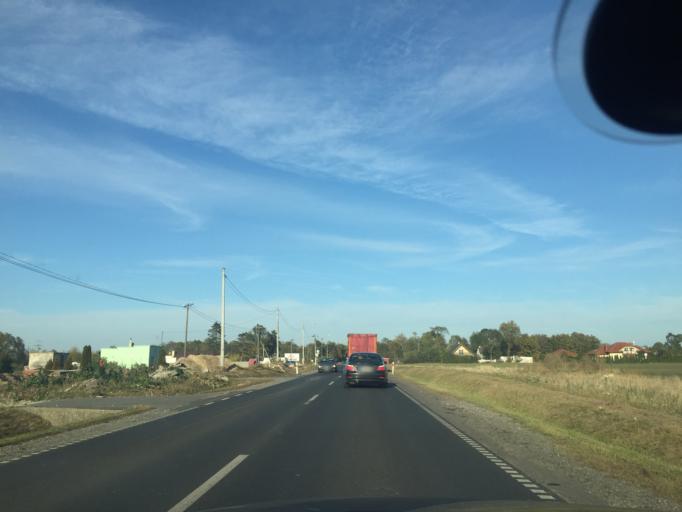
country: PL
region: Kujawsko-Pomorskie
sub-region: Powiat inowroclawski
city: Inowroclaw
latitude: 52.8234
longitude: 18.3014
